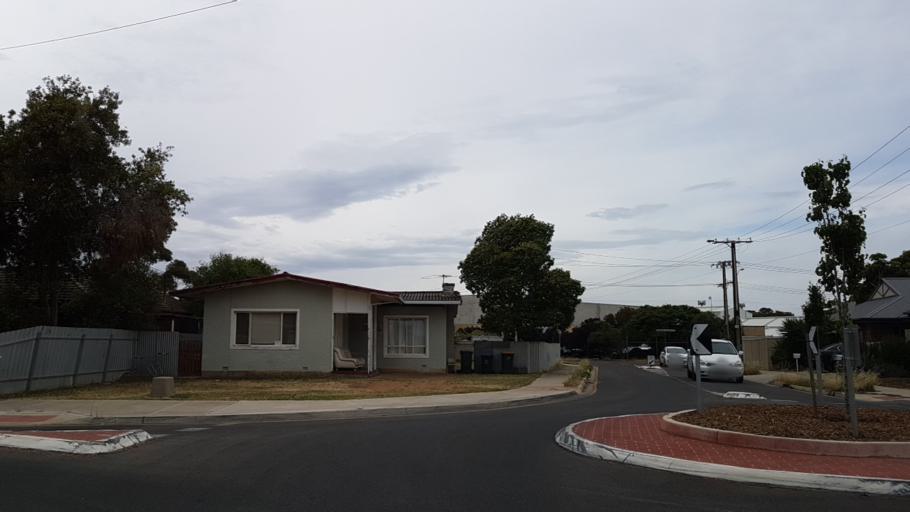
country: AU
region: South Australia
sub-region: Charles Sturt
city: Findon
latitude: -34.8984
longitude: 138.5410
